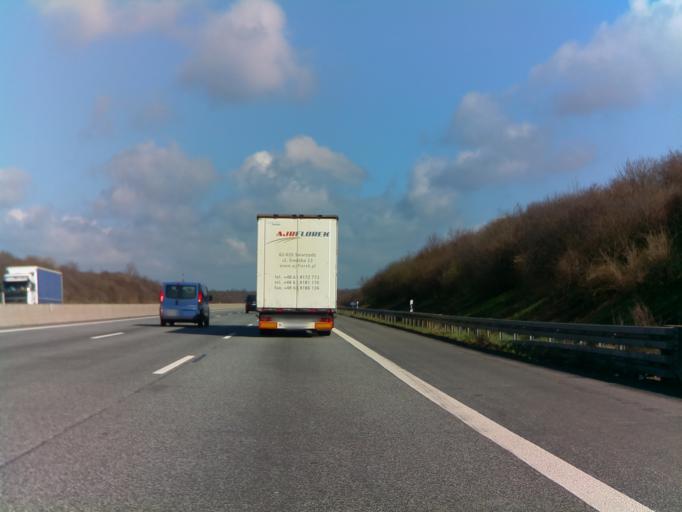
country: DE
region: Saxony-Anhalt
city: Raguhn
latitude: 51.7185
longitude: 12.2145
